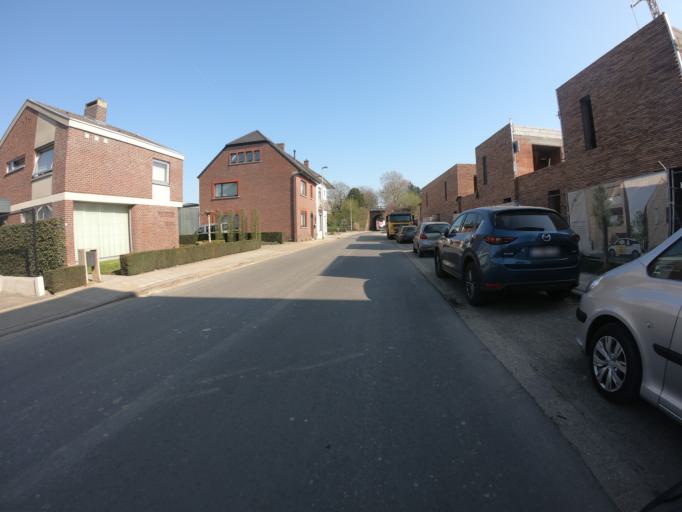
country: BE
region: Flanders
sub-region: Provincie Limburg
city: Sint-Truiden
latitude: 50.8233
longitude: 5.1820
